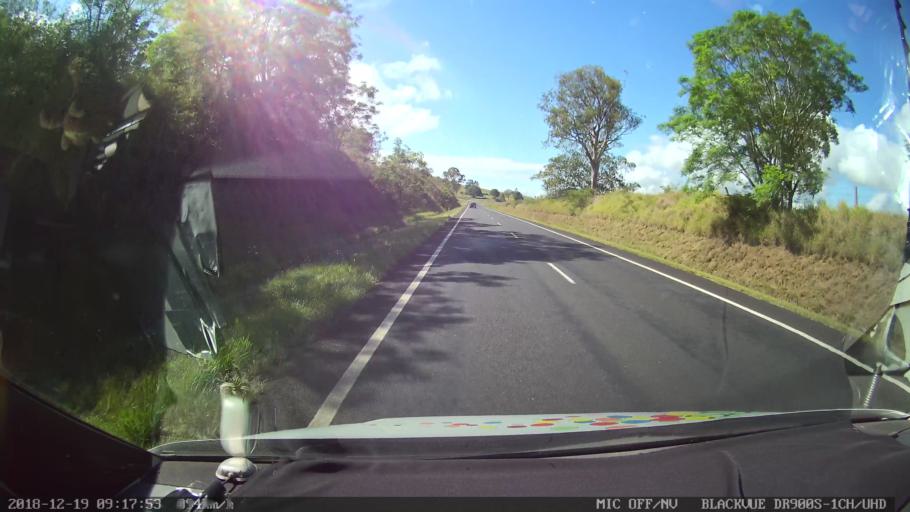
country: AU
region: New South Wales
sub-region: Kyogle
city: Kyogle
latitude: -28.5400
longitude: 152.9756
